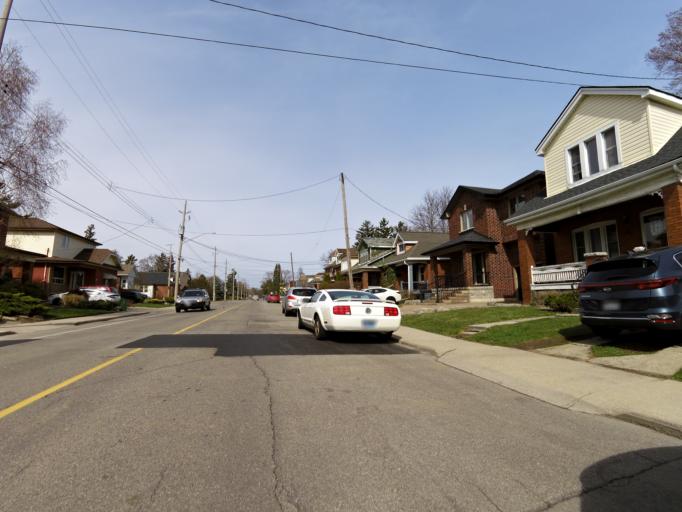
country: CA
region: Ontario
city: Hamilton
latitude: 43.2651
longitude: -79.8998
